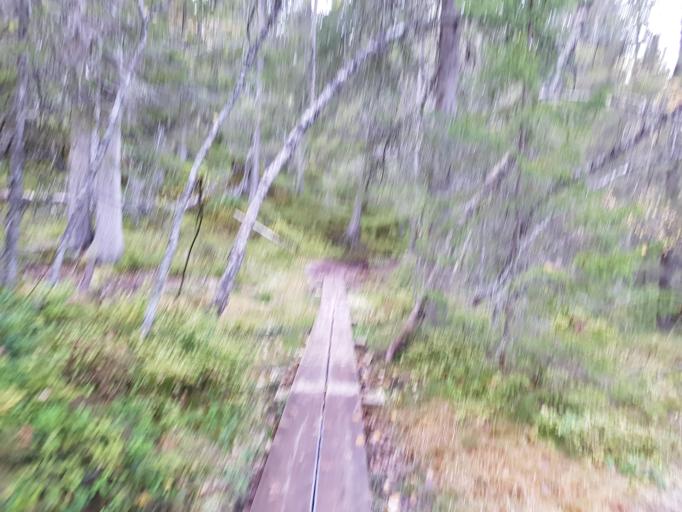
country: NO
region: Sor-Trondelag
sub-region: Trondheim
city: Trondheim
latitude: 63.4480
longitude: 10.2703
